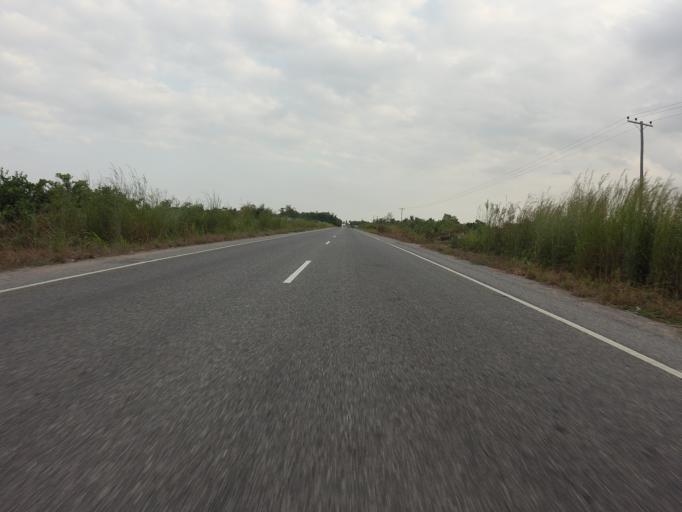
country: GH
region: Volta
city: Ho
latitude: 6.2404
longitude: 0.5510
